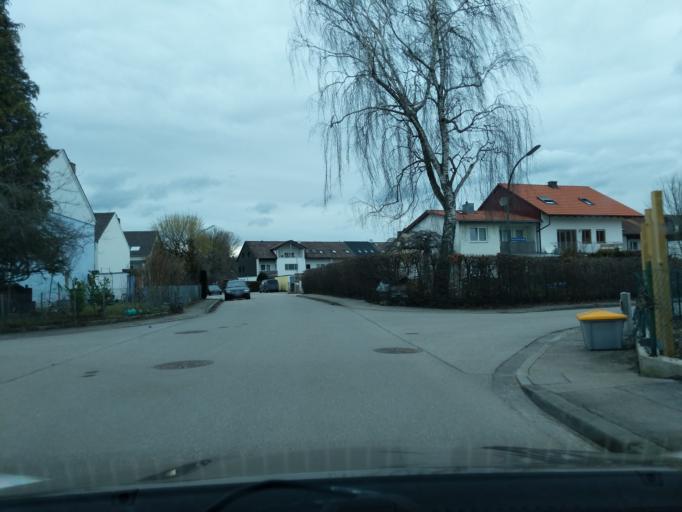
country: DE
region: Bavaria
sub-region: Upper Bavaria
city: Grafing bei Munchen
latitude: 48.0517
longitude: 11.9593
